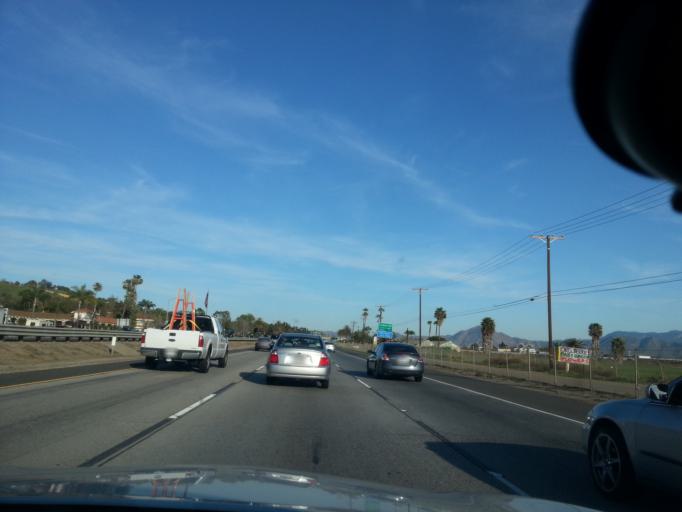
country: US
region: California
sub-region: Ventura County
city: El Rio
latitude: 34.2220
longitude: -119.1086
